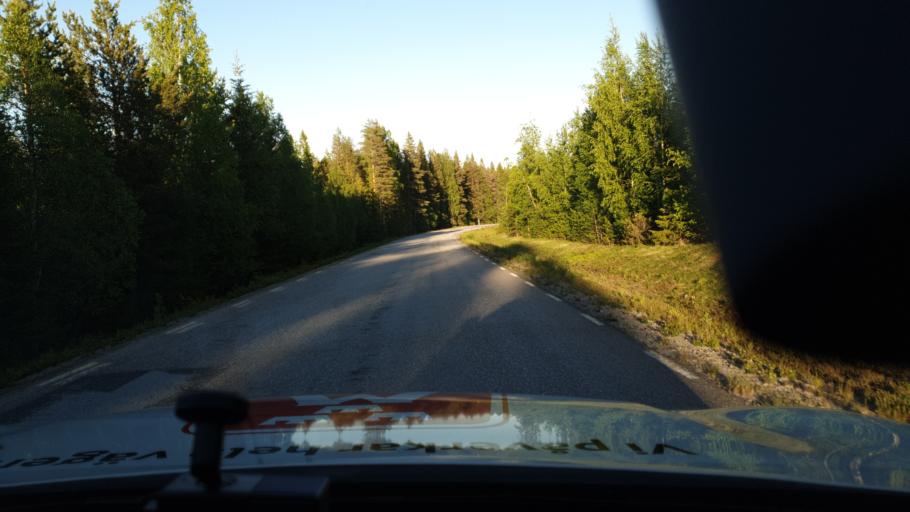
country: SE
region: Vaesterbotten
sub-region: Umea Kommun
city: Ersmark
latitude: 64.0104
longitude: 20.1864
